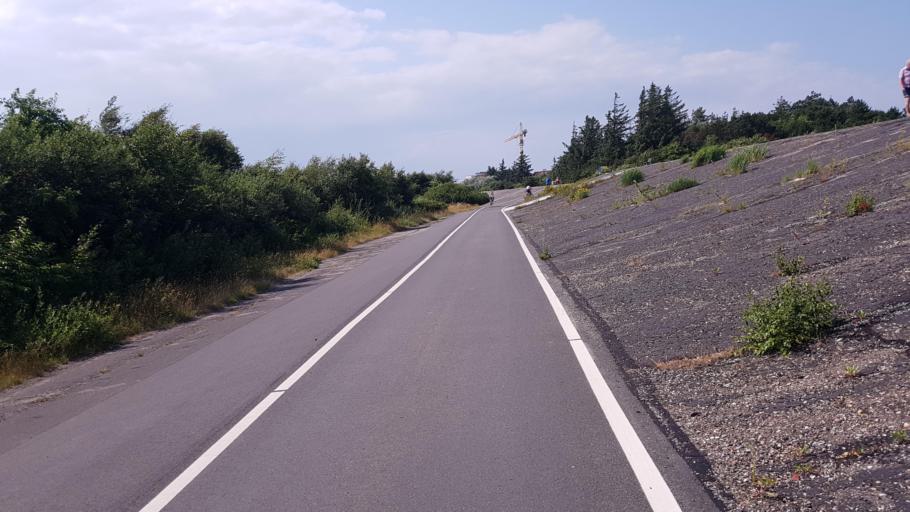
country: DE
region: Schleswig-Holstein
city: Sankt Peter-Ording
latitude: 54.3050
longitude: 8.6224
